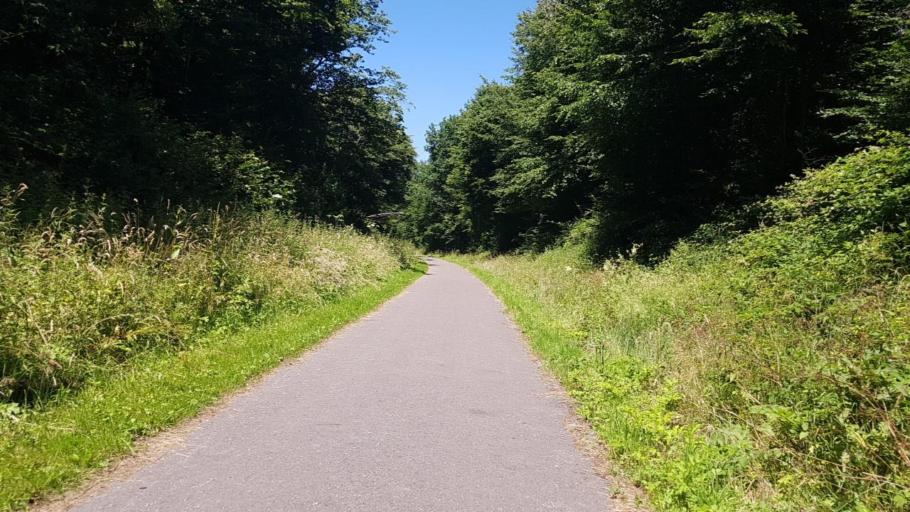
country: BE
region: Wallonia
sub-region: Province du Hainaut
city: Froidchapelle
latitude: 50.1525
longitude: 4.2726
